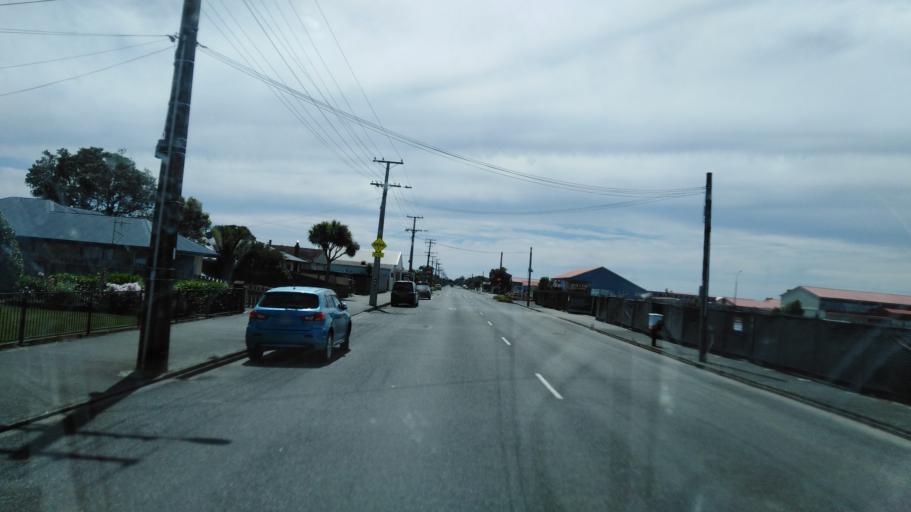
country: NZ
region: West Coast
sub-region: Buller District
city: Westport
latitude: -41.7493
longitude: 171.6046
